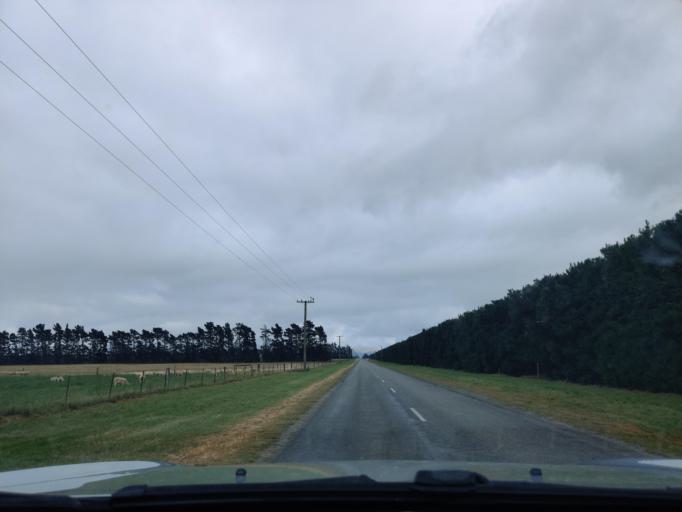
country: NZ
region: Canterbury
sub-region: Hurunui District
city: Amberley
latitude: -43.0782
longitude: 172.7369
